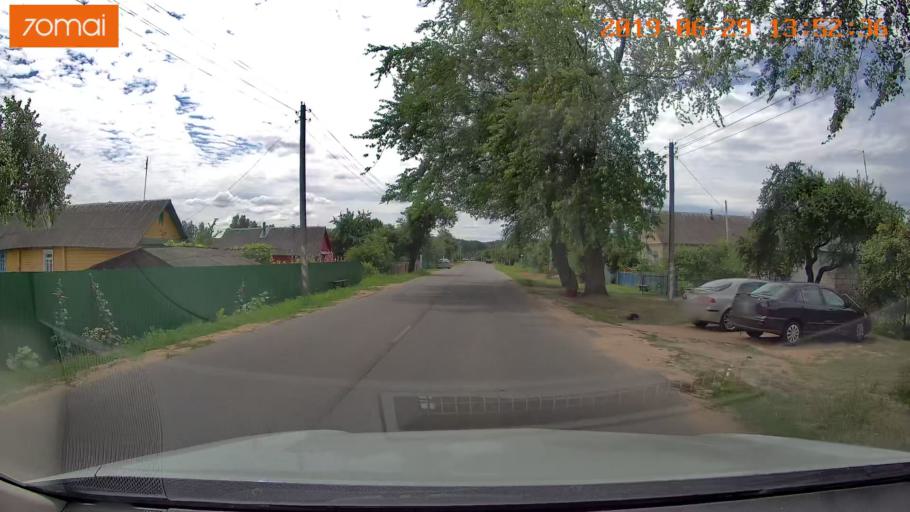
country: BY
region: Minsk
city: Slutsk
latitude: 52.9944
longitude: 27.5533
